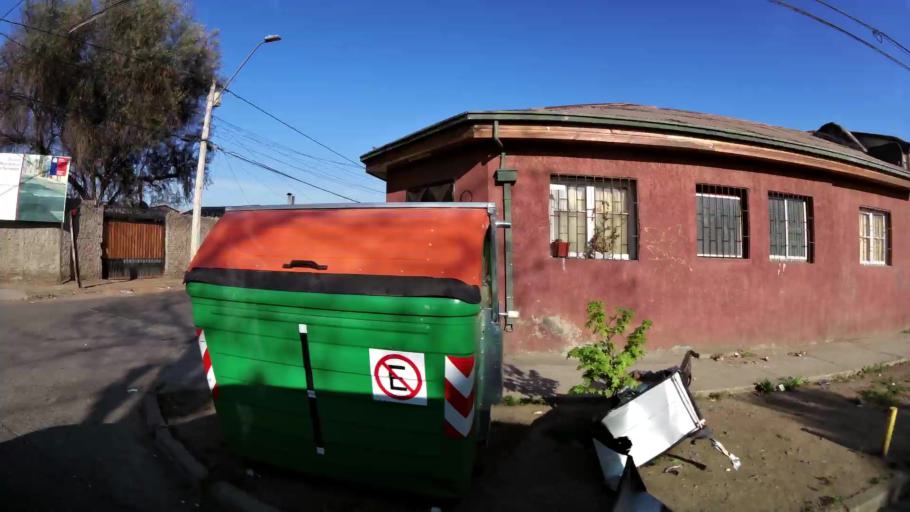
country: CL
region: Santiago Metropolitan
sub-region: Provincia de Santiago
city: Santiago
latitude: -33.3735
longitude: -70.6694
